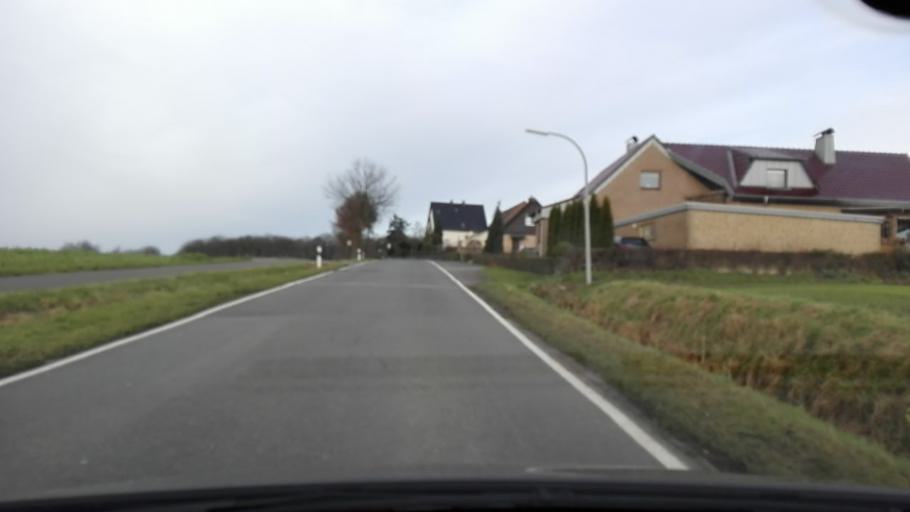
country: DE
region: North Rhine-Westphalia
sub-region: Regierungsbezirk Arnsberg
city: Holzwickede
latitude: 51.4838
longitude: 7.6524
